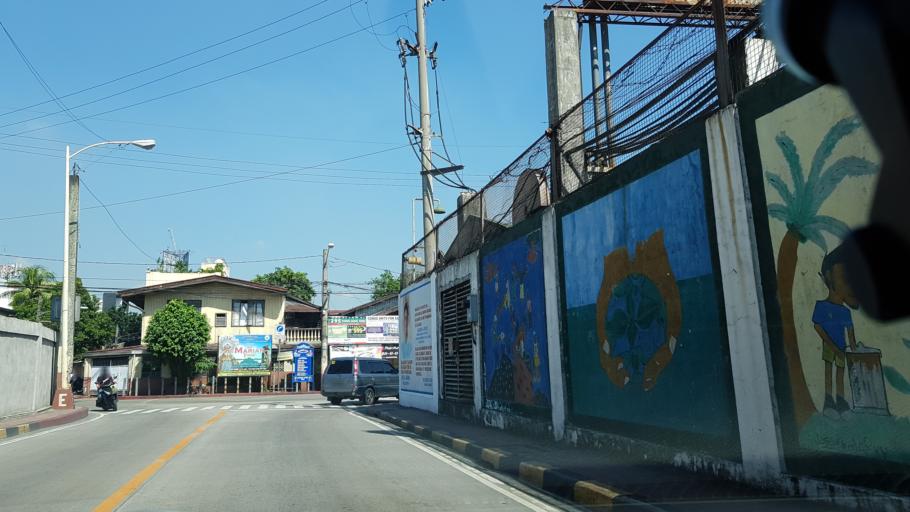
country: PH
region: Calabarzon
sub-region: Province of Rizal
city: Pateros
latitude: 14.5613
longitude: 121.0709
